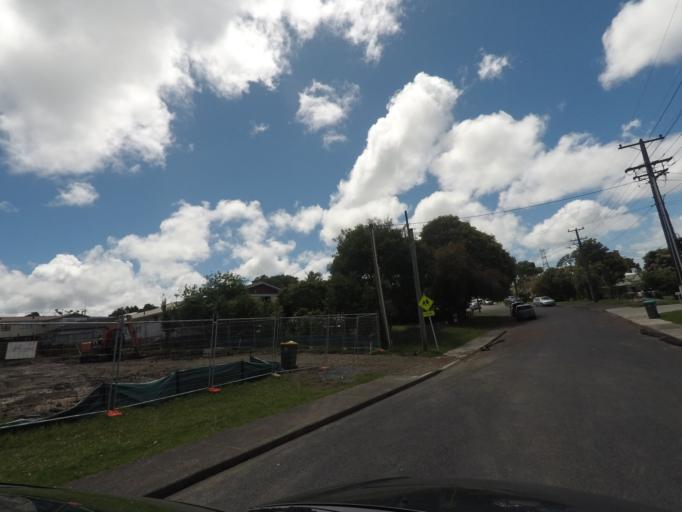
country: NZ
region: Auckland
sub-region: Auckland
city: Rosebank
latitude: -36.8717
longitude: 174.6482
